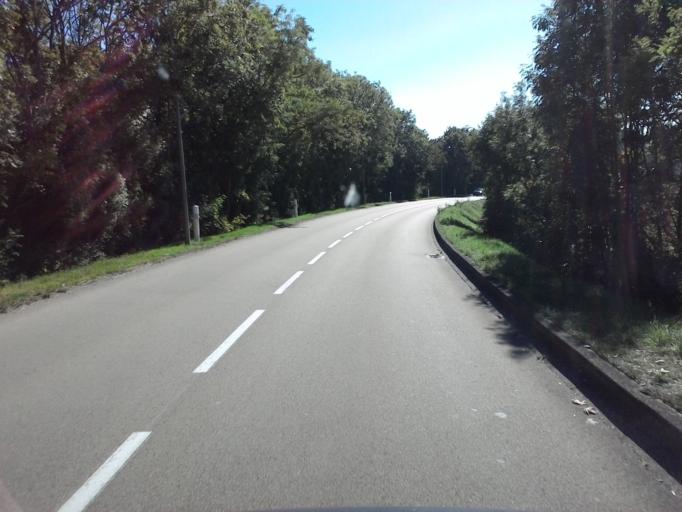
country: FR
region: Champagne-Ardenne
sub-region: Departement de la Haute-Marne
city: Chaumont
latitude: 48.1219
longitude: 5.1483
